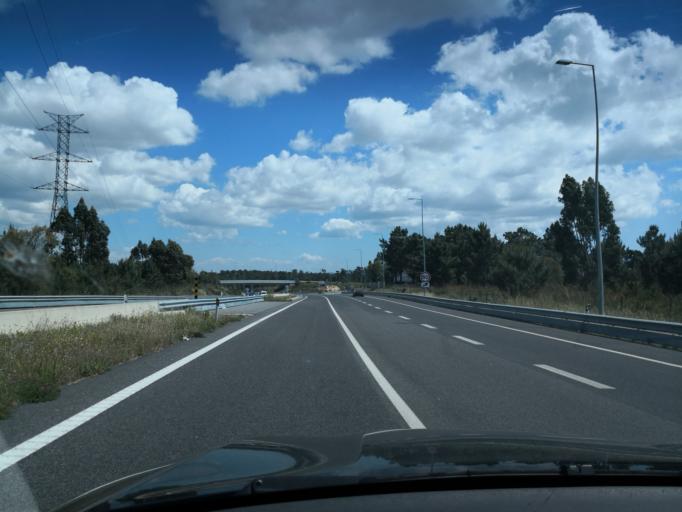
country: PT
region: Setubal
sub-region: Seixal
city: Amora
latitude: 38.6043
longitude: -9.1336
